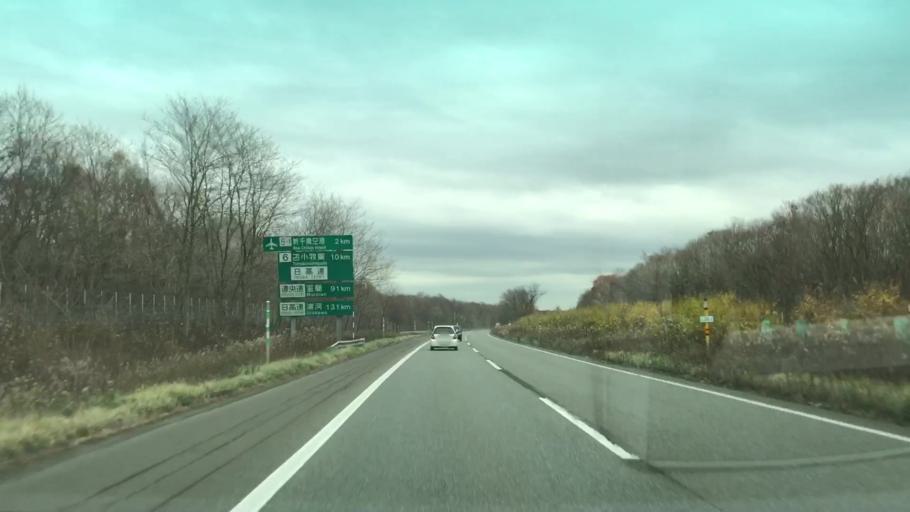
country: JP
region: Hokkaido
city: Chitose
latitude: 42.8003
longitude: 141.6259
